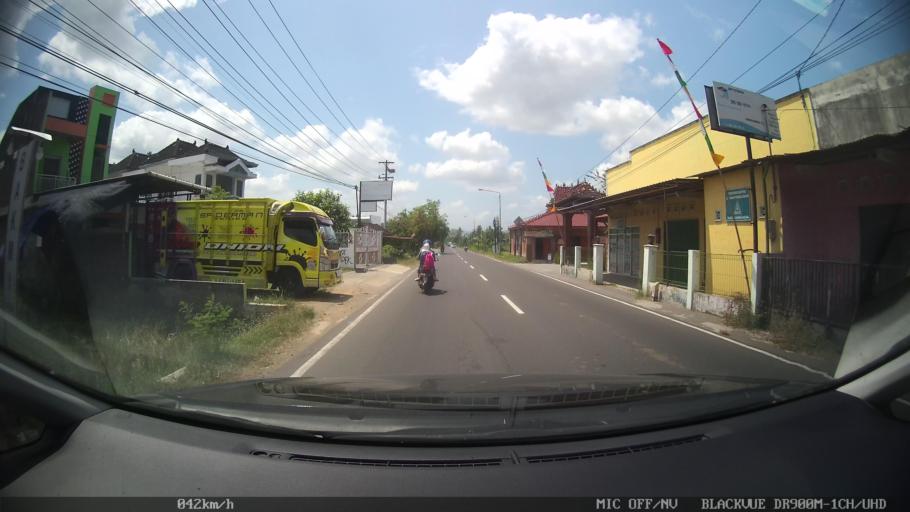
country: ID
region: Daerah Istimewa Yogyakarta
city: Bantul
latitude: -7.9051
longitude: 110.3225
